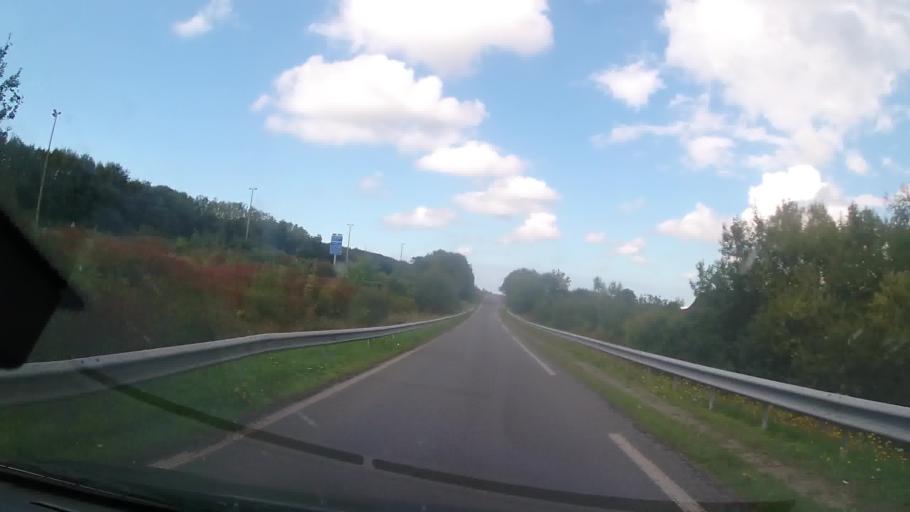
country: FR
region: Nord-Pas-de-Calais
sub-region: Departement du Pas-de-Calais
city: Saint-Martin-Boulogne
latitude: 50.7424
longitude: 1.6295
